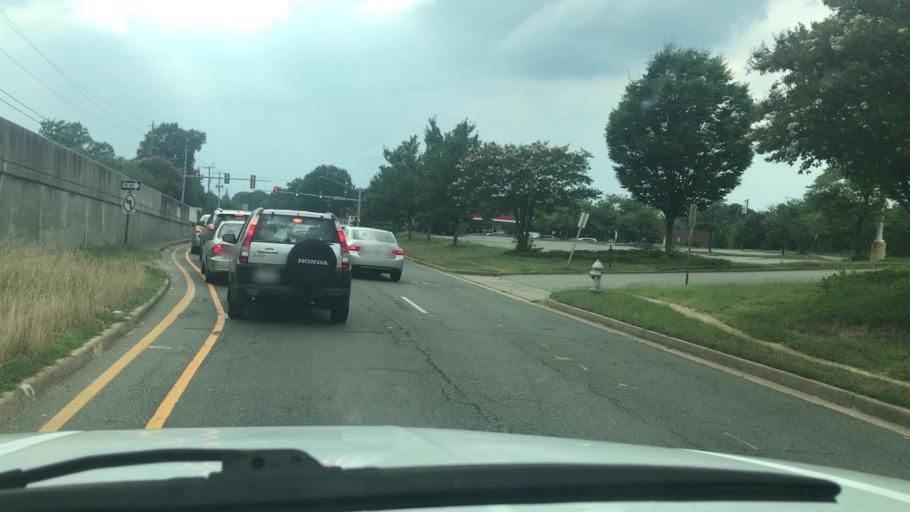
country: US
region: Virginia
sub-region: Henrico County
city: Tuckahoe
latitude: 37.6040
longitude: -77.5678
